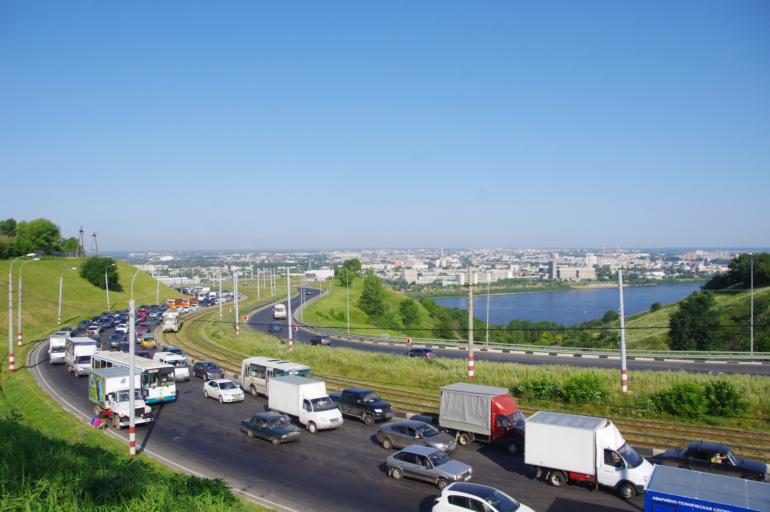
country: RU
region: Nizjnij Novgorod
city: Nizhniy Novgorod
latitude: 56.3036
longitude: 43.9769
